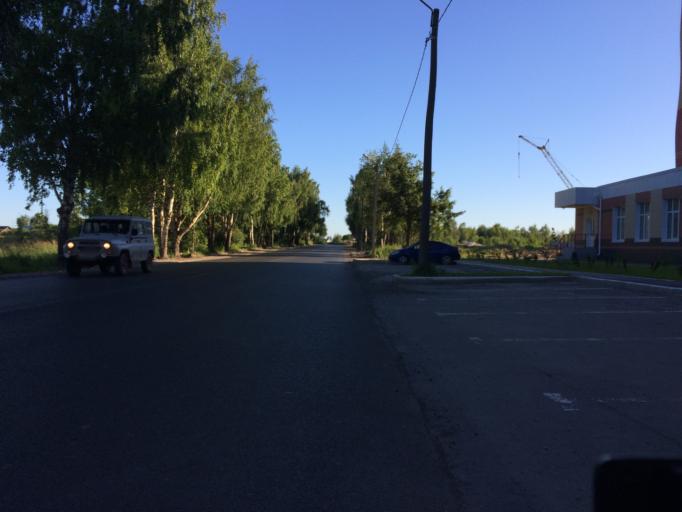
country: RU
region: Mariy-El
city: Medvedevo
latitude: 56.6469
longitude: 47.8311
